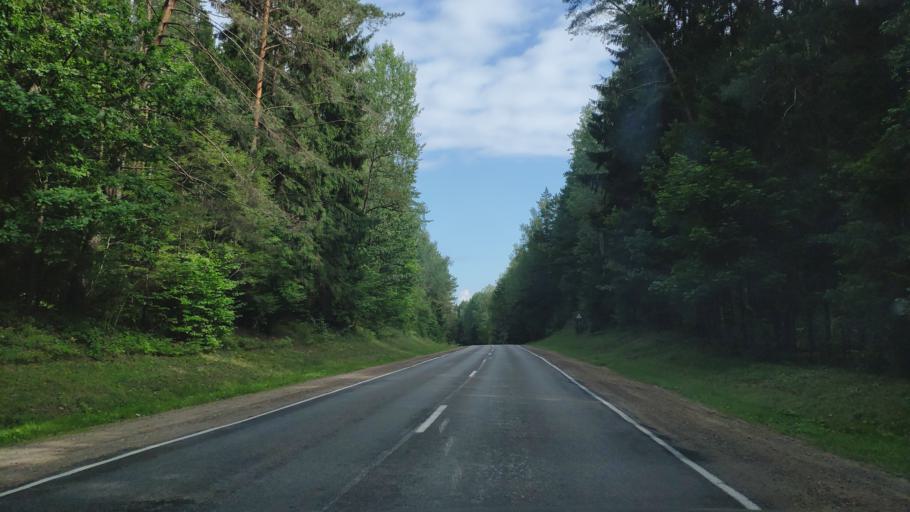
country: BY
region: Minsk
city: Novosel'ye
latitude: 53.9502
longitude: 27.2458
